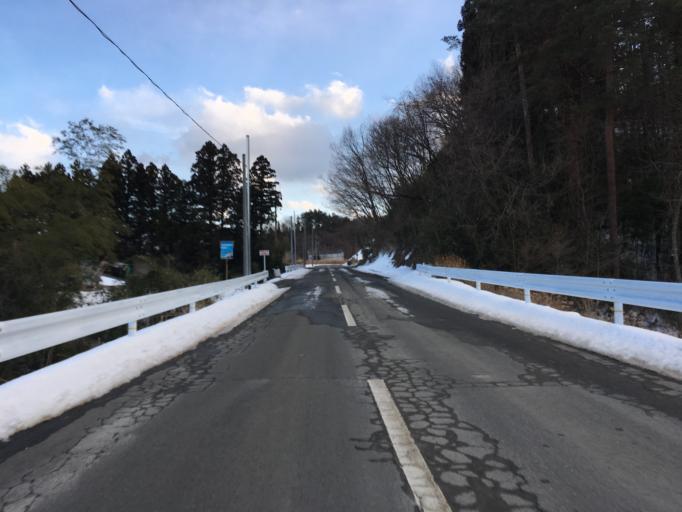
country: JP
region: Fukushima
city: Fukushima-shi
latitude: 37.6430
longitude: 140.5865
